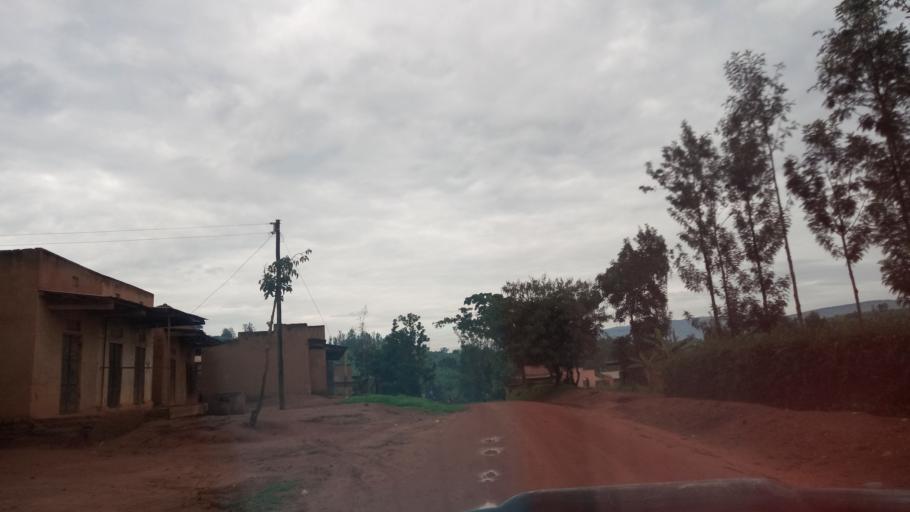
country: UG
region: Western Region
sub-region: Buhweju District
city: Buhweju
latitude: -0.1711
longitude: 30.4616
